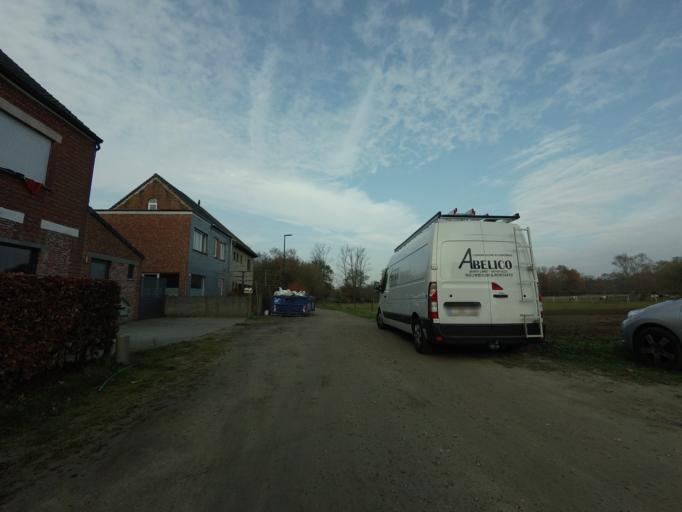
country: BE
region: Flanders
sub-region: Provincie Vlaams-Brabant
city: Boortmeerbeek
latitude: 51.0026
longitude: 4.5829
